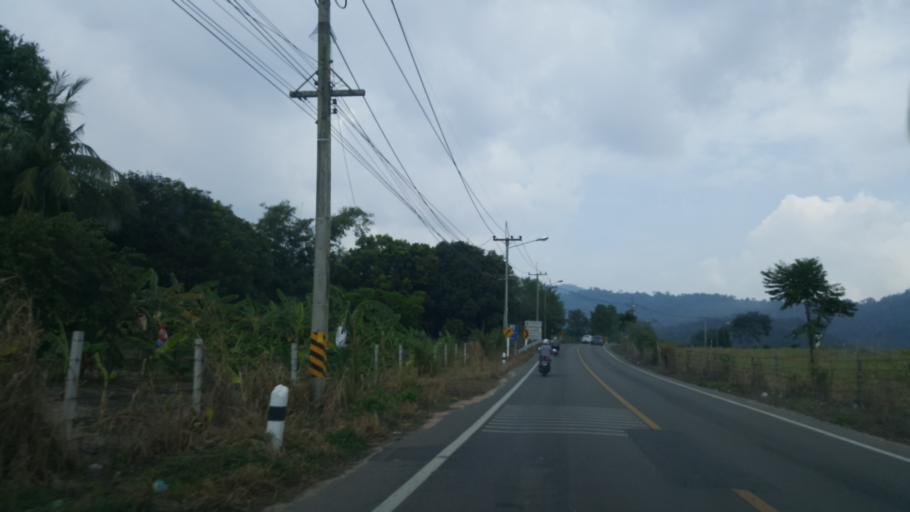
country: TH
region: Chon Buri
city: Si Racha
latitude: 13.2118
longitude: 101.0405
